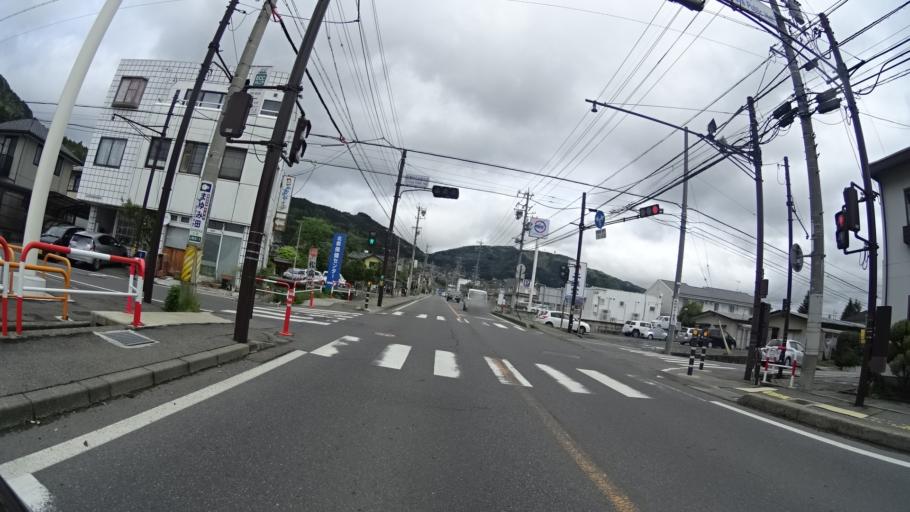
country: JP
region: Nagano
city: Nagano-shi
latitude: 36.6775
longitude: 138.2003
